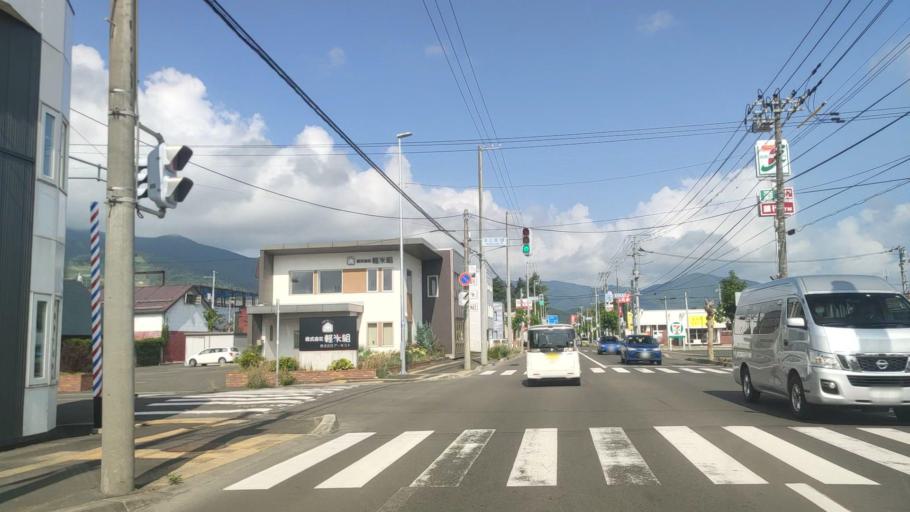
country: JP
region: Hokkaido
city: Shimo-furano
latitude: 43.3423
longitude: 142.3858
